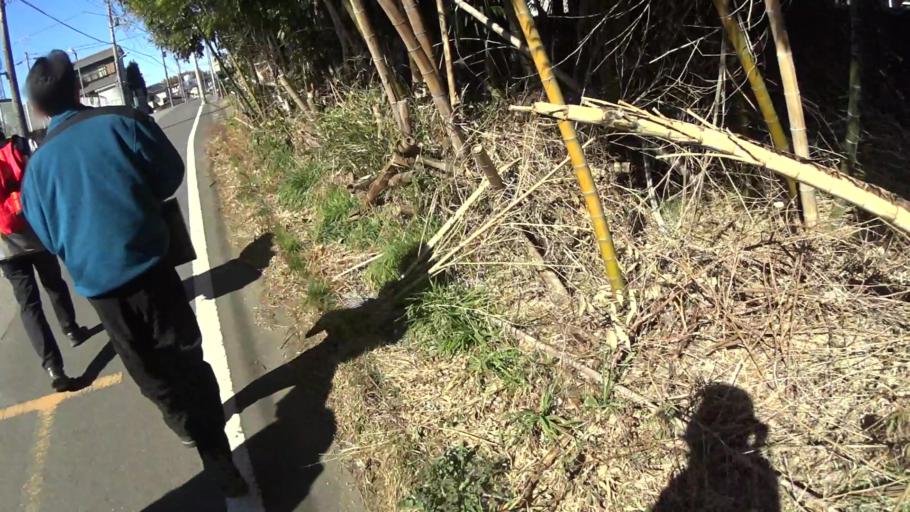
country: JP
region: Saitama
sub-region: Kawaguchi-shi
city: Hatogaya-honcho
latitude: 35.8530
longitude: 139.7495
